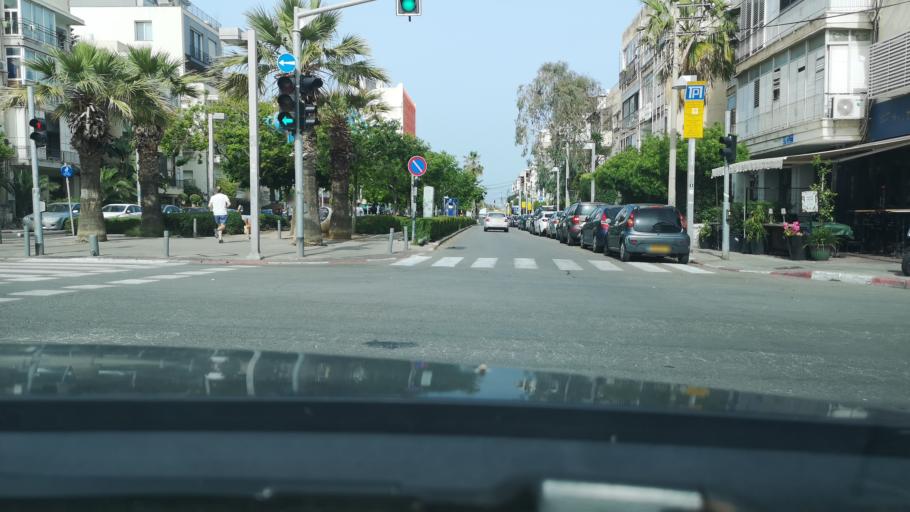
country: IL
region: Tel Aviv
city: Tel Aviv
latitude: 32.0924
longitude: 34.7764
